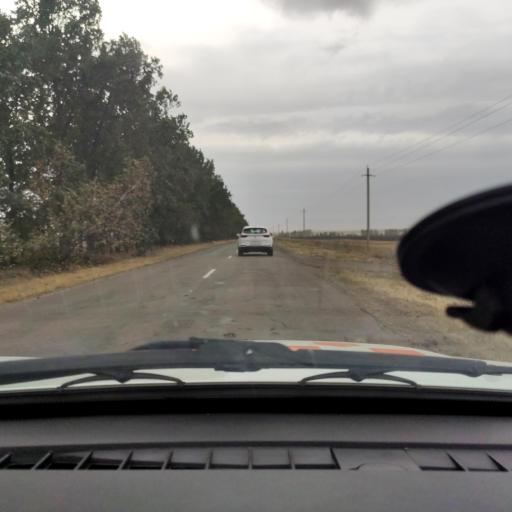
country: RU
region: Lipetsk
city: Khlevnoye
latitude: 52.0060
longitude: 39.1454
